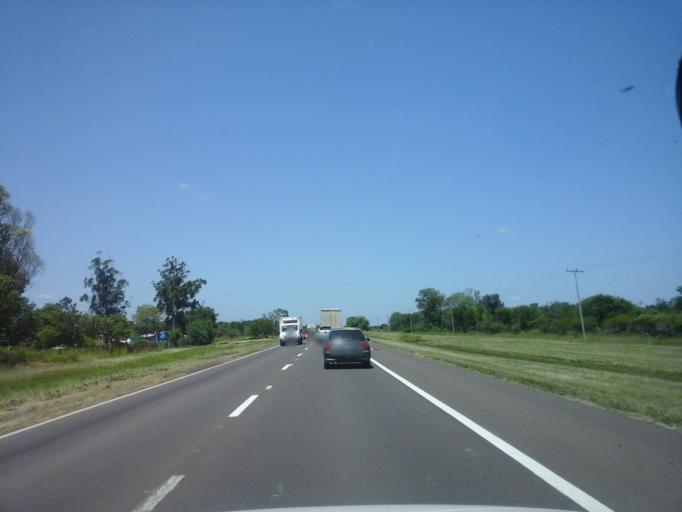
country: AR
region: Corrientes
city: Paso de la Patria
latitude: -27.4036
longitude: -58.6381
